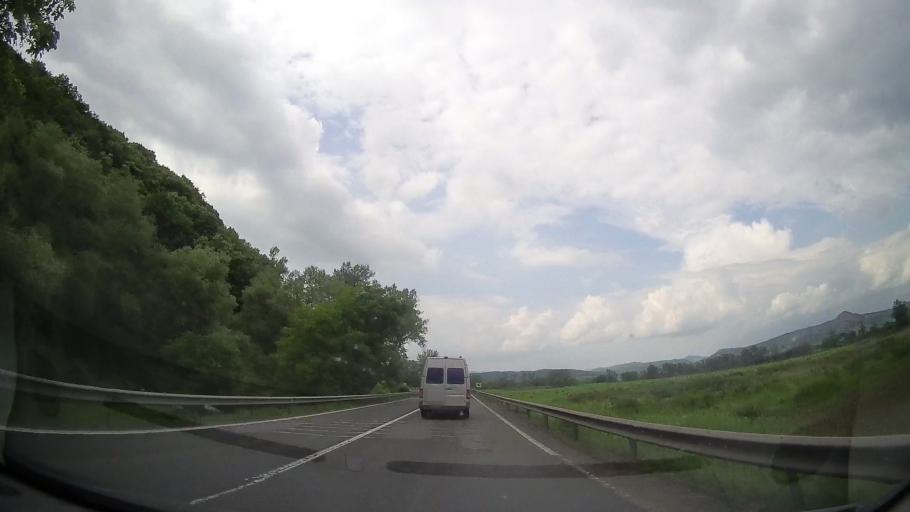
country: RO
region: Hunedoara
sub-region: Comuna Ilia
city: Ilia
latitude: 45.9226
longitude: 22.7005
